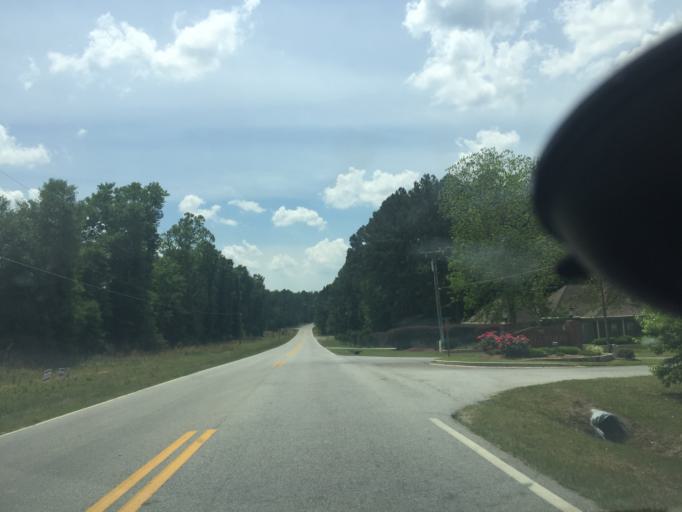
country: US
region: Georgia
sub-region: Bulloch County
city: Statesboro
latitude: 32.4180
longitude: -81.8208
